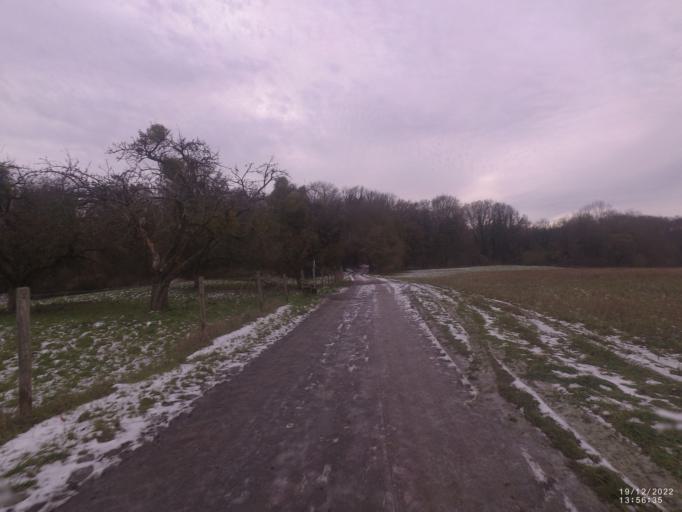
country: DE
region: Rheinland-Pfalz
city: Unkel
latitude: 50.6098
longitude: 7.1862
